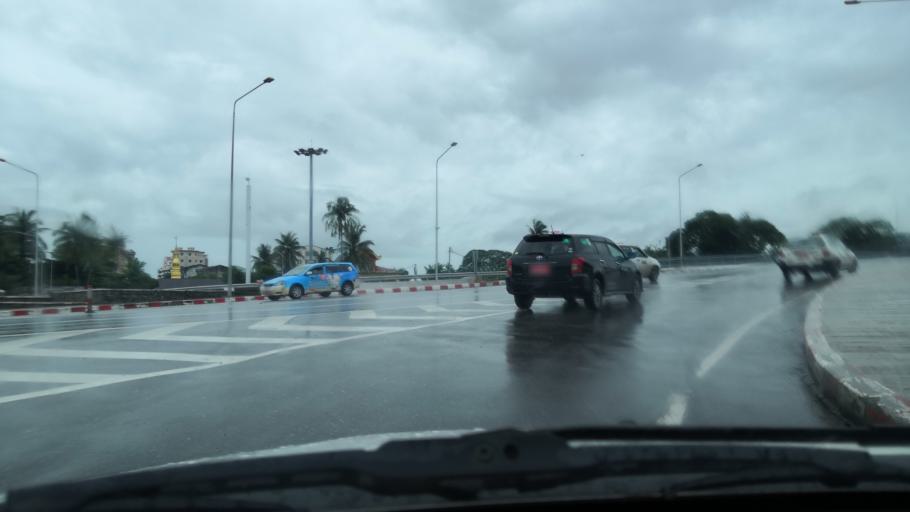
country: MM
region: Yangon
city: Yangon
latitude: 16.7869
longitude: 96.1775
